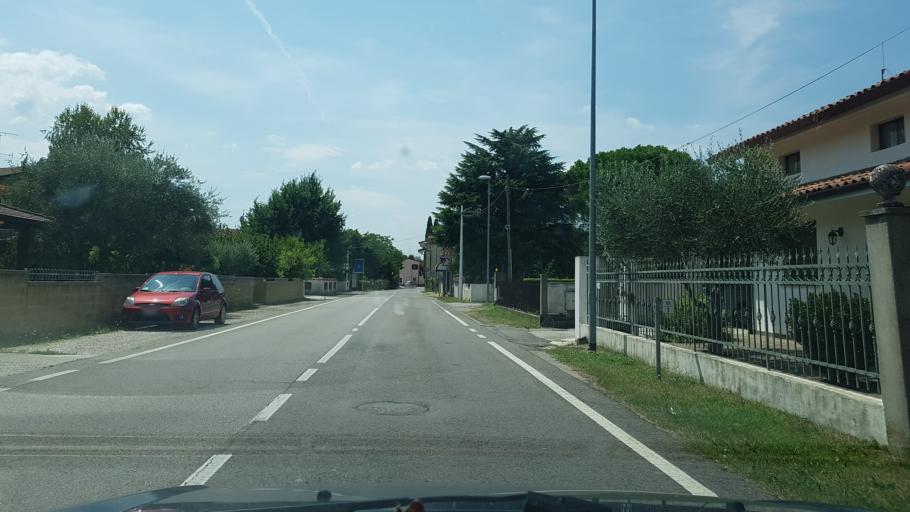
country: IT
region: Friuli Venezia Giulia
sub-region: Provincia di Gorizia
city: Medea
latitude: 45.9091
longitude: 13.4408
